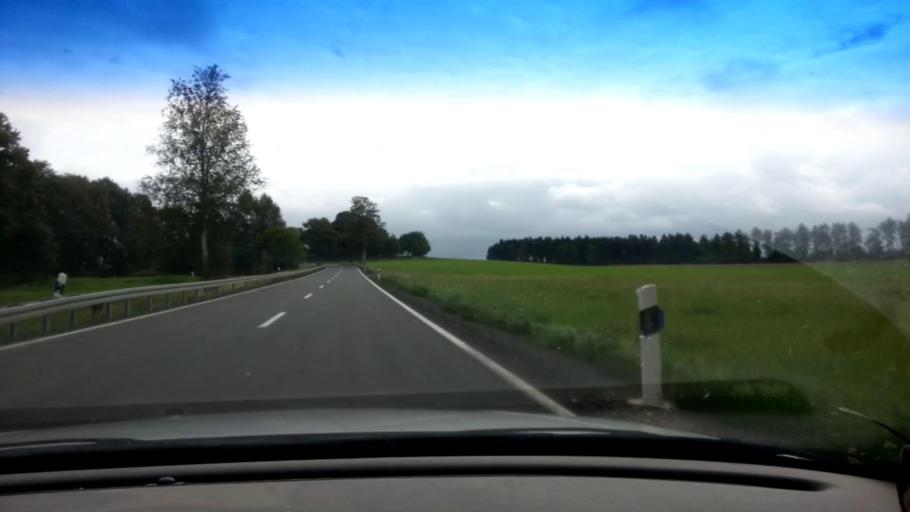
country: DE
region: Bavaria
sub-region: Upper Franconia
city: Wunsiedel
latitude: 50.0741
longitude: 12.0379
